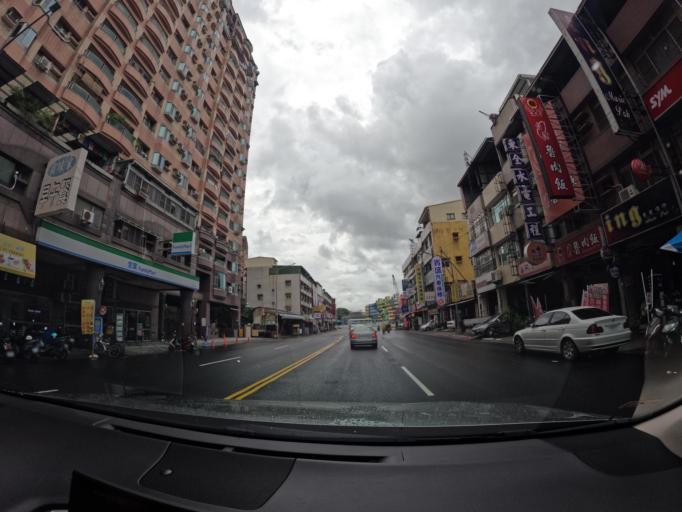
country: TW
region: Taiwan
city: Fengshan
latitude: 22.6287
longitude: 120.3415
